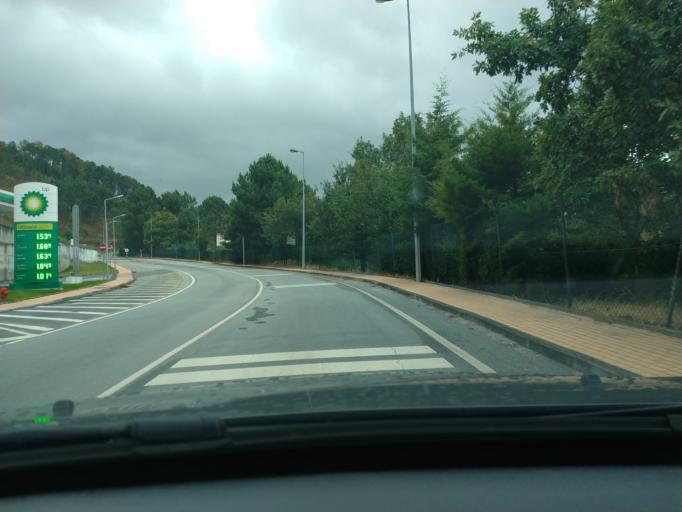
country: PT
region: Guarda
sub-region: Seia
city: Seia
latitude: 40.4073
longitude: -7.7093
